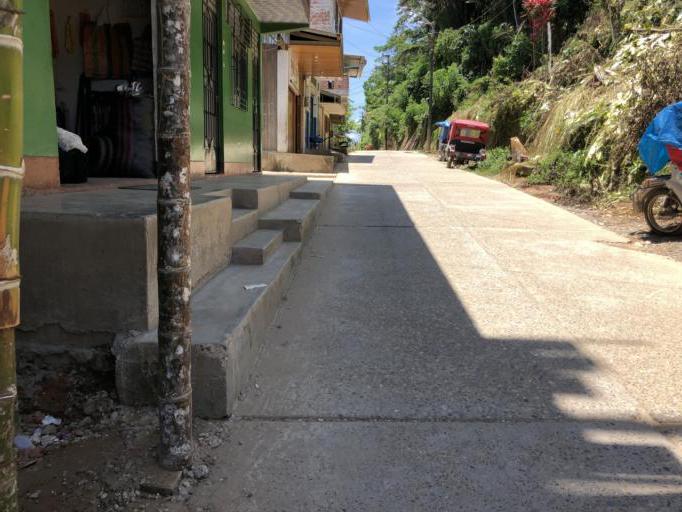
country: PE
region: Loreto
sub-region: Datem Del Maranon
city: Saramiriza
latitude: -4.5946
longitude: -77.8653
